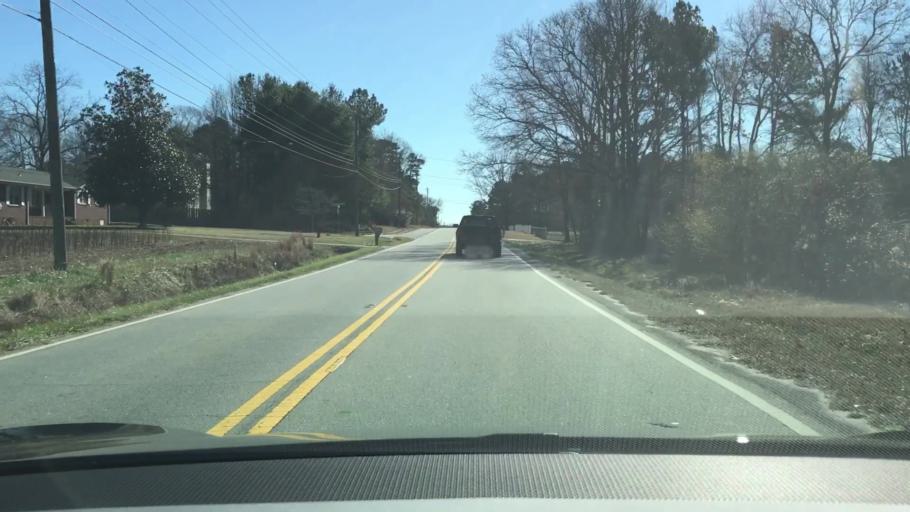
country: US
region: Georgia
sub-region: Gwinnett County
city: Dacula
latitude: 33.9665
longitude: -83.8864
